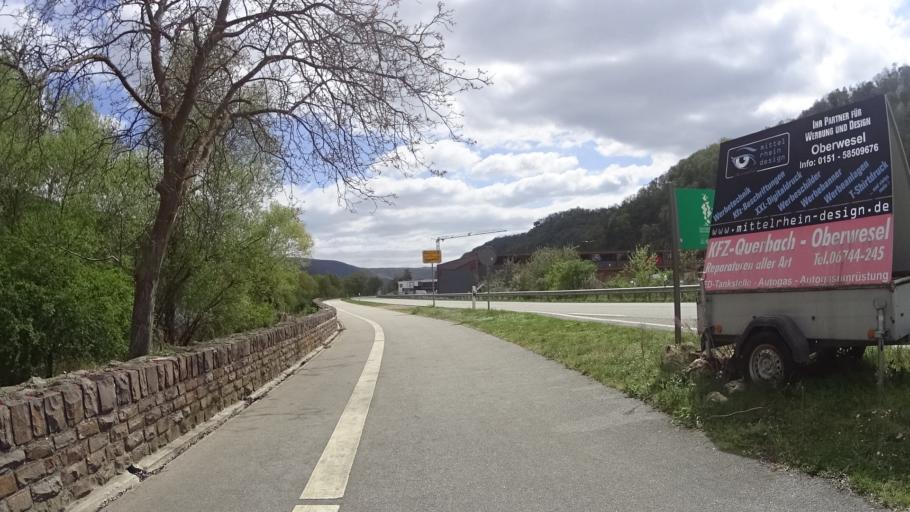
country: DE
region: Rheinland-Pfalz
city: Dorscheid
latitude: 50.1015
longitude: 7.7379
